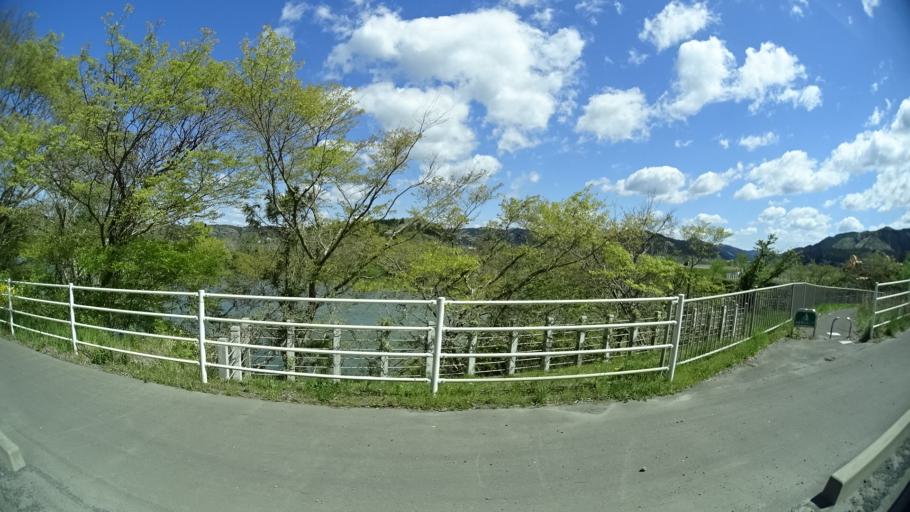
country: JP
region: Miyagi
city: Wakuya
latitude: 38.6019
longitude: 141.2892
